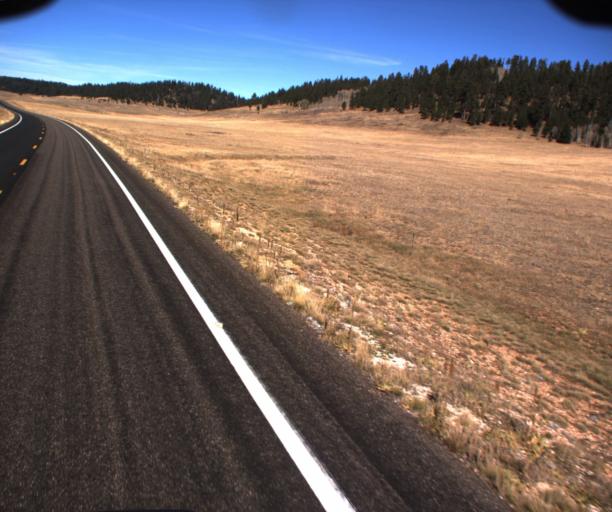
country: US
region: Arizona
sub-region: Coconino County
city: Grand Canyon
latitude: 36.4764
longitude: -112.1258
